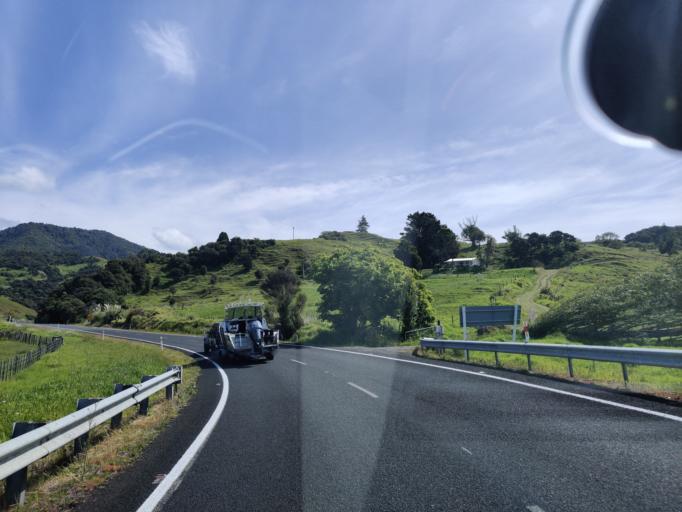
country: NZ
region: Northland
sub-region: Far North District
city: Kaitaia
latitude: -35.4749
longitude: 173.4592
